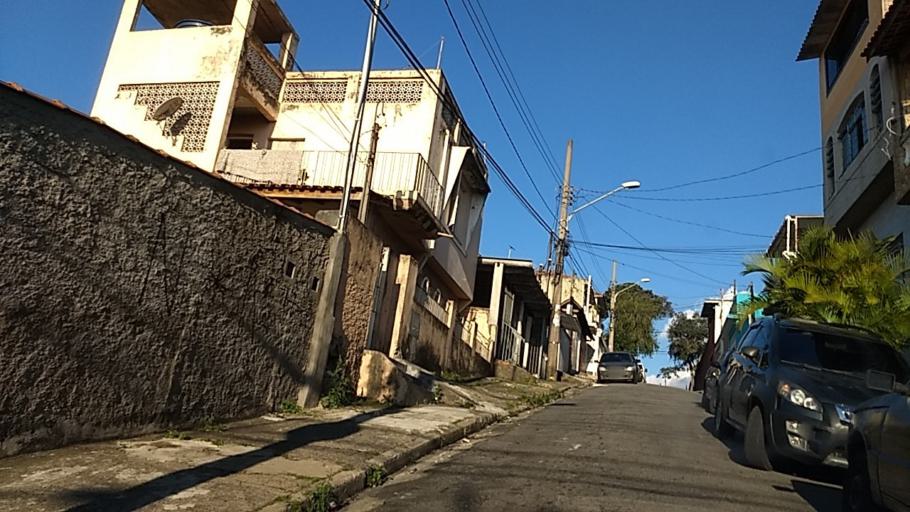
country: BR
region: Sao Paulo
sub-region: Guarulhos
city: Guarulhos
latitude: -23.4941
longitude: -46.5883
